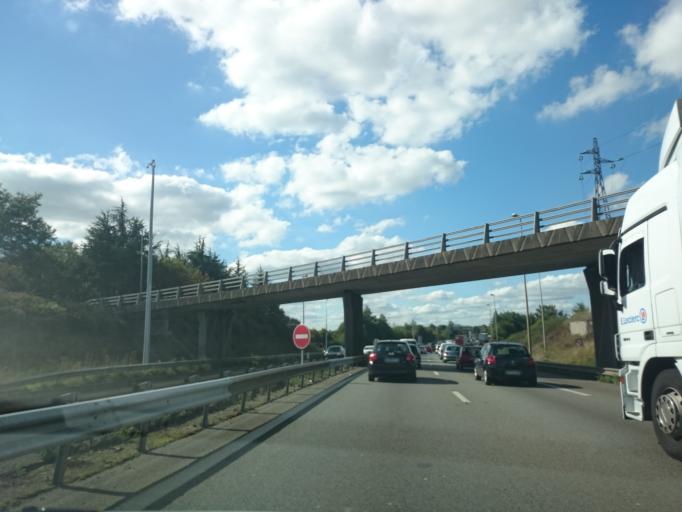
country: FR
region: Pays de la Loire
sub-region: Departement de la Loire-Atlantique
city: Bouguenais
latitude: 47.2010
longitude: -1.6196
